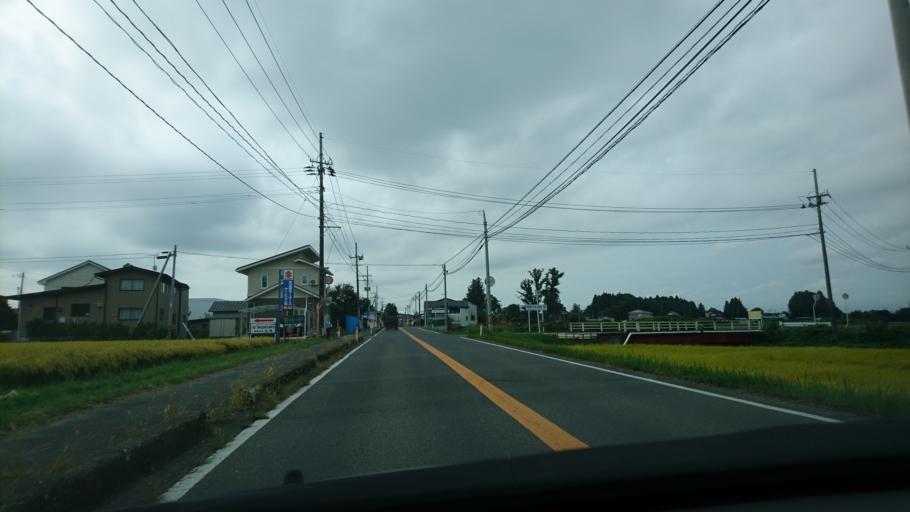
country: JP
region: Miyagi
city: Furukawa
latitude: 38.7394
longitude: 141.0355
